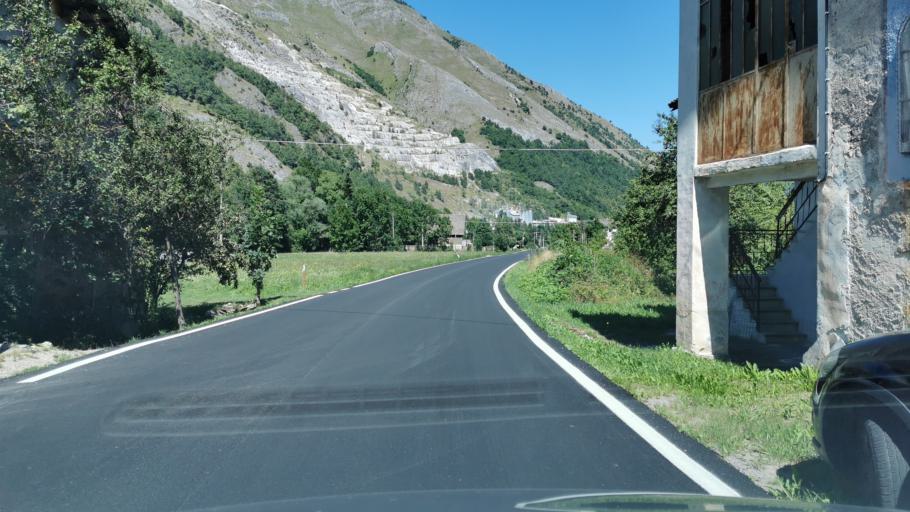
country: IT
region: Piedmont
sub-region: Provincia di Cuneo
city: Entracque
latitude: 44.2573
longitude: 7.3540
